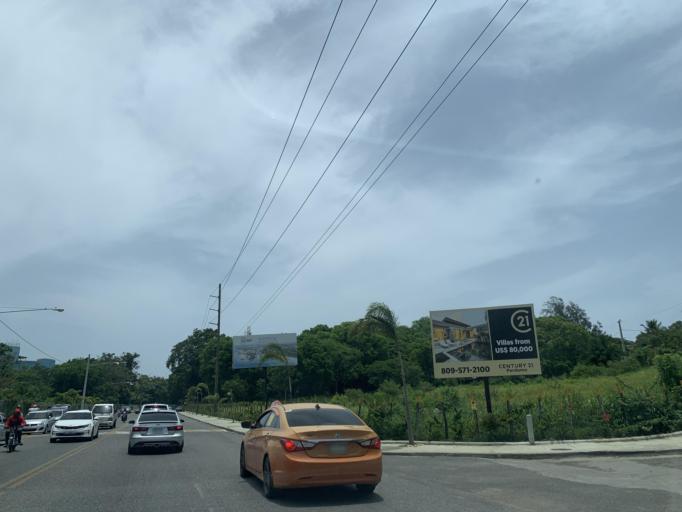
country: DO
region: Puerto Plata
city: Cabarete
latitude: 19.7602
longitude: -70.5159
